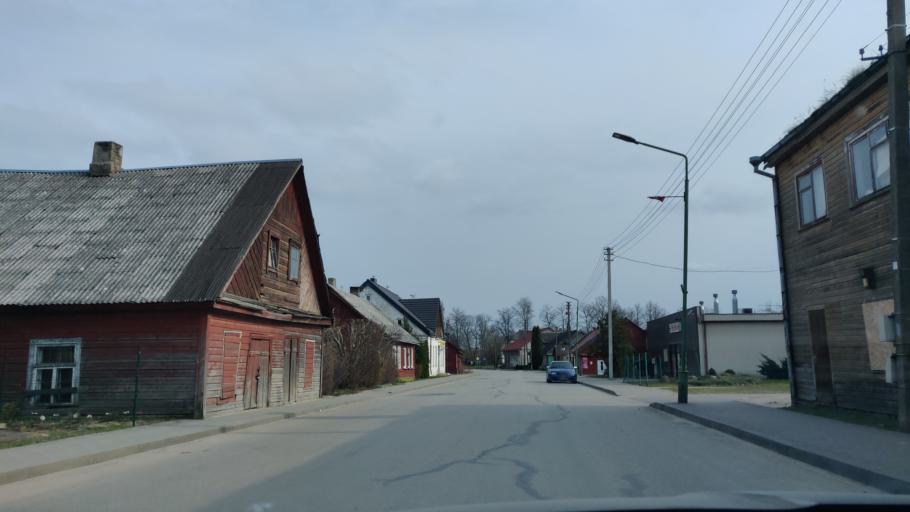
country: LT
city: Jieznas
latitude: 54.5999
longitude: 24.1693
